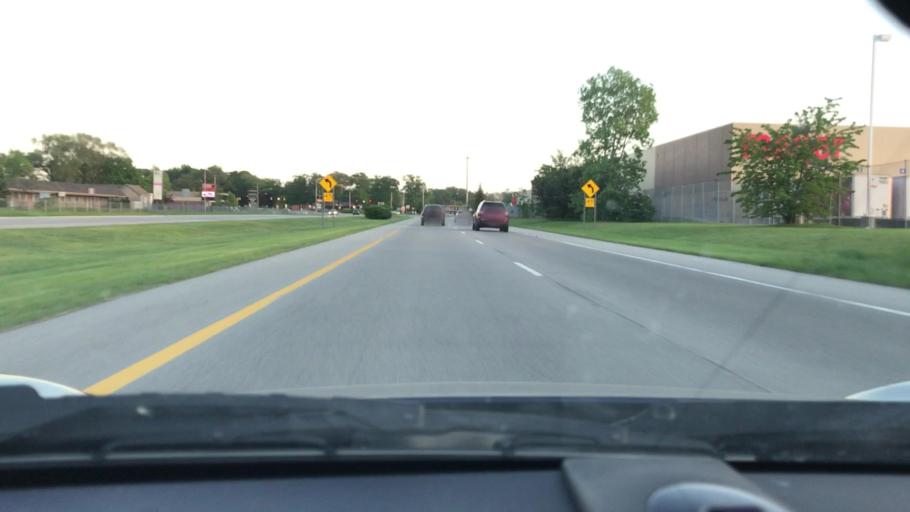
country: US
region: Michigan
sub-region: Muskegon County
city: Roosevelt Park
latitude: 43.1943
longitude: -86.2603
